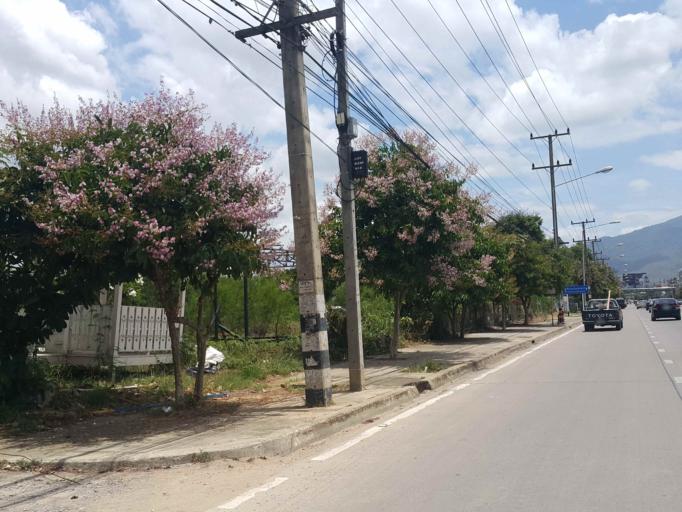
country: TH
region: Chiang Mai
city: Chiang Mai
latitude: 18.7659
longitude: 98.9894
